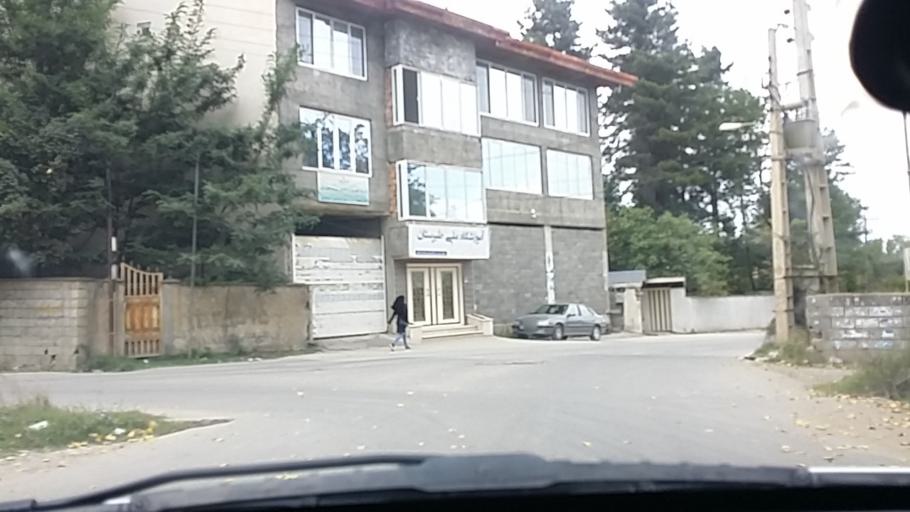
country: IR
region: Mazandaran
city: `Abbasabad
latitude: 36.5036
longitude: 51.1613
